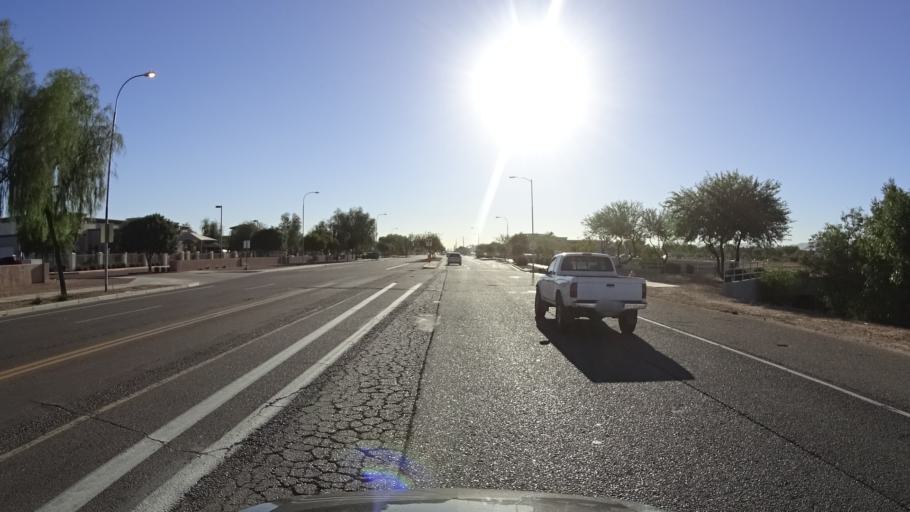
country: US
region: Arizona
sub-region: Maricopa County
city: Tolleson
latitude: 33.4229
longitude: -112.2279
